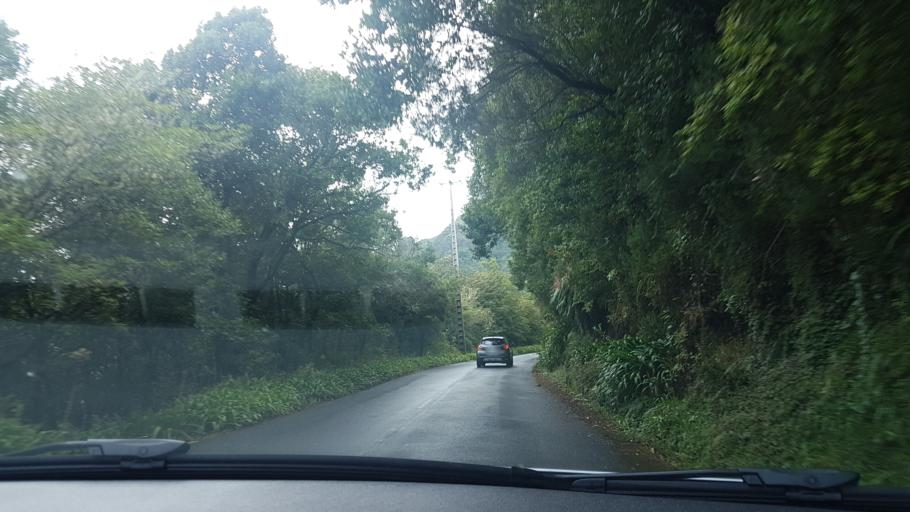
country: PT
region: Madeira
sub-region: Sao Vicente
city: Sao Vicente
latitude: 32.7621
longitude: -17.0179
